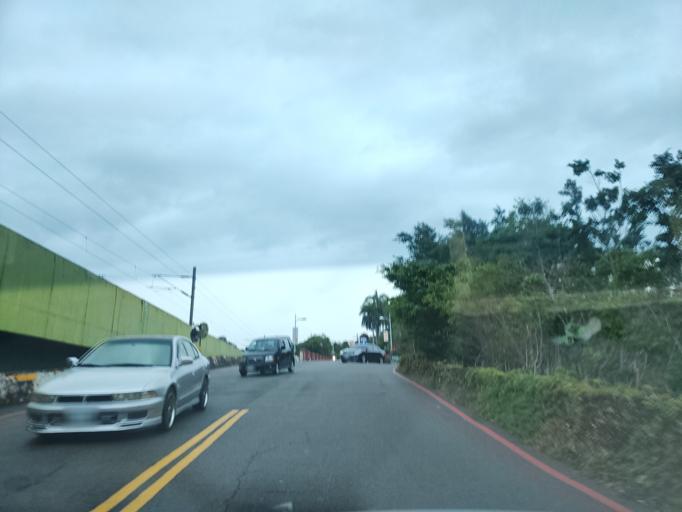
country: TW
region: Taiwan
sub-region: Miaoli
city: Miaoli
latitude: 24.5564
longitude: 120.8144
